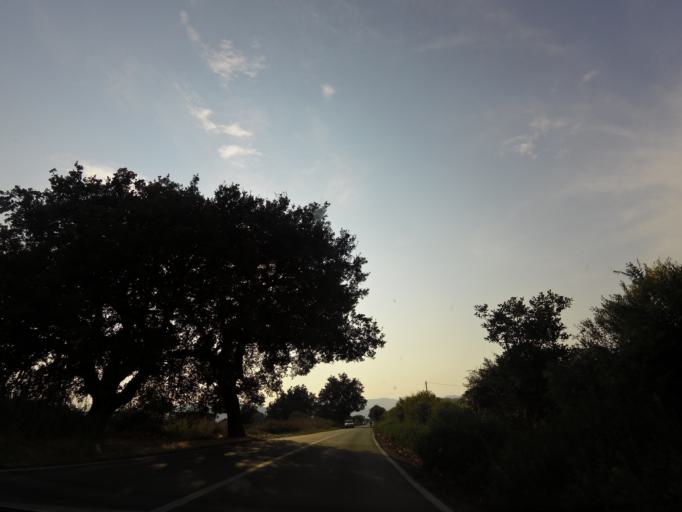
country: IT
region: Calabria
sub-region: Provincia di Reggio Calabria
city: Monasterace Marina
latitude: 38.4358
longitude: 16.5619
